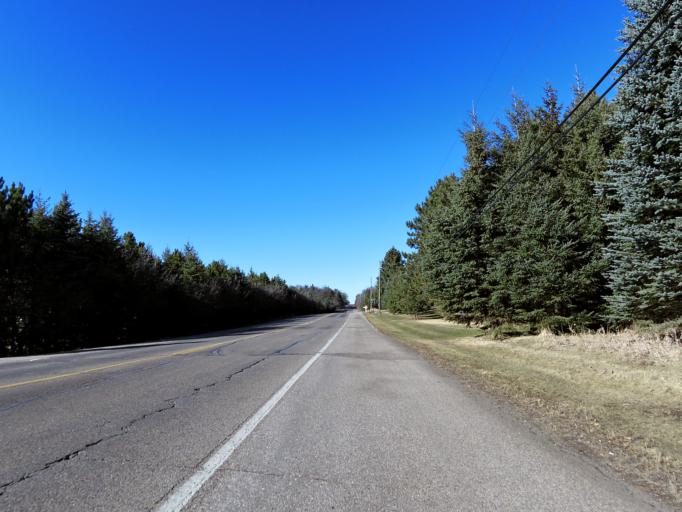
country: US
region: Minnesota
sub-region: Washington County
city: Lakeland
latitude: 44.9750
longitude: -92.8223
